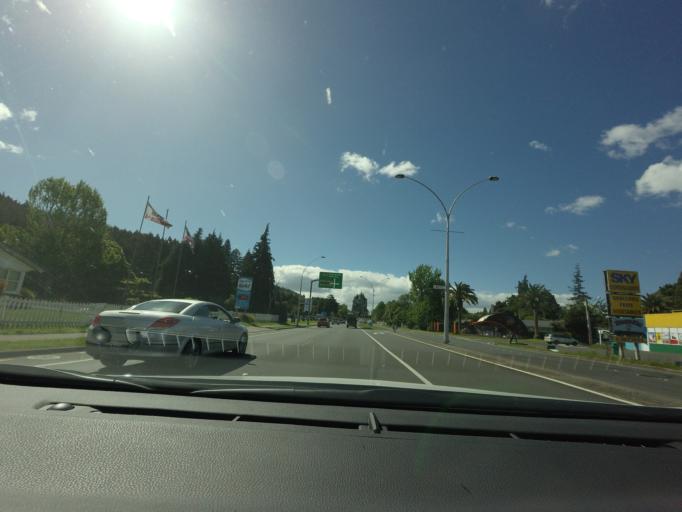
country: NZ
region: Bay of Plenty
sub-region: Rotorua District
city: Rotorua
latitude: -38.1110
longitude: 176.2237
